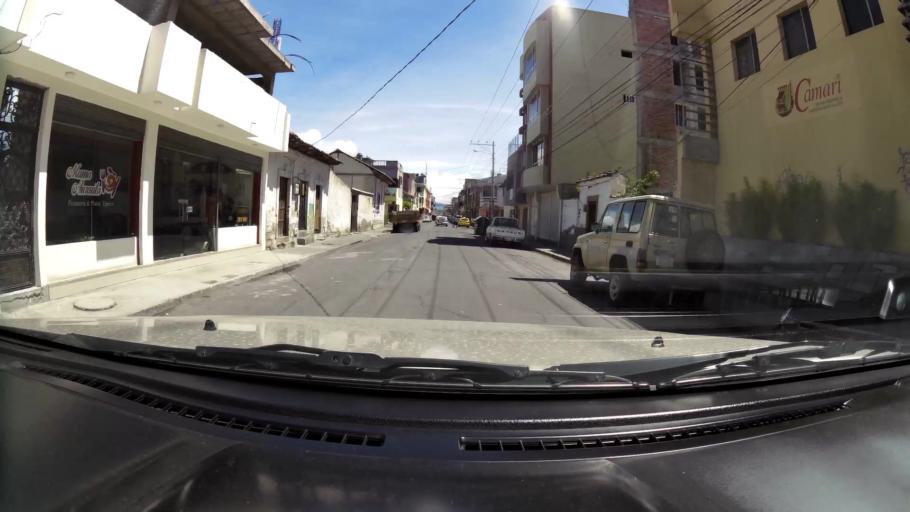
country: EC
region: Chimborazo
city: Riobamba
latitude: -1.6764
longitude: -78.6499
